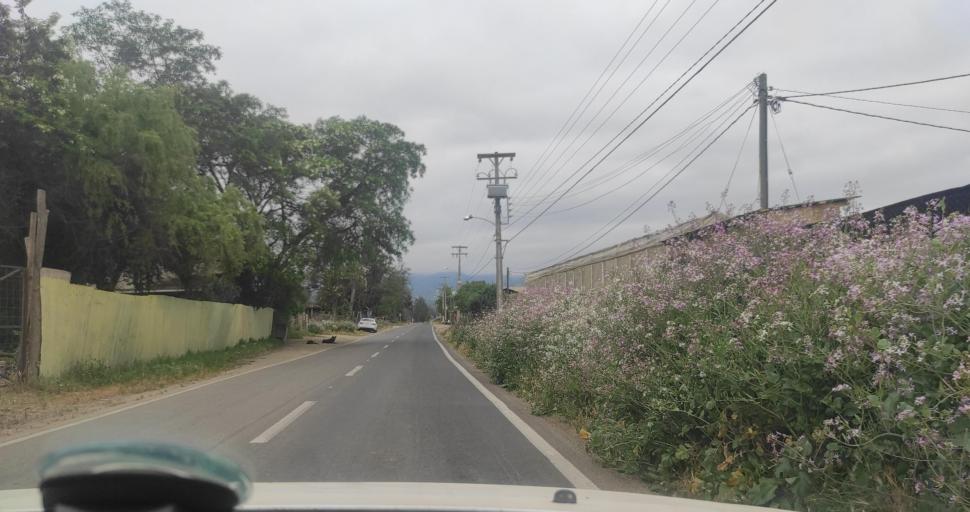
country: CL
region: Valparaiso
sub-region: Provincia de Marga Marga
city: Limache
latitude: -33.0185
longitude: -71.2334
